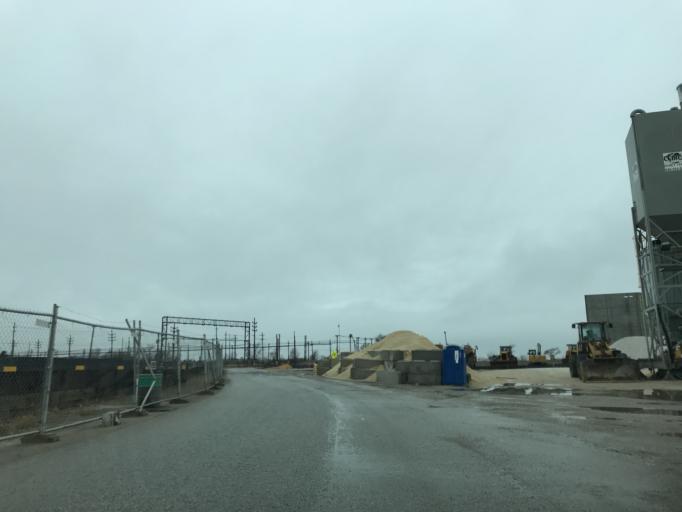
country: US
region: Maryland
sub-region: Baltimore County
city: Dundalk
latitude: 39.2313
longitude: -76.4881
